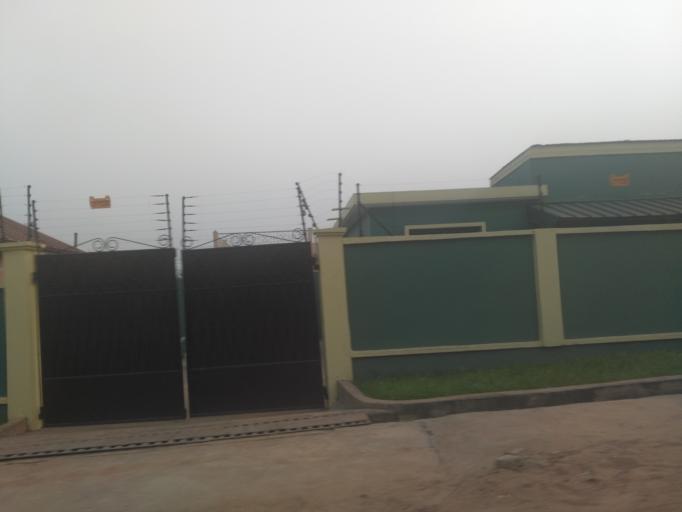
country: GH
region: Ashanti
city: Kumasi
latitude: 6.6701
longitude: -1.6014
